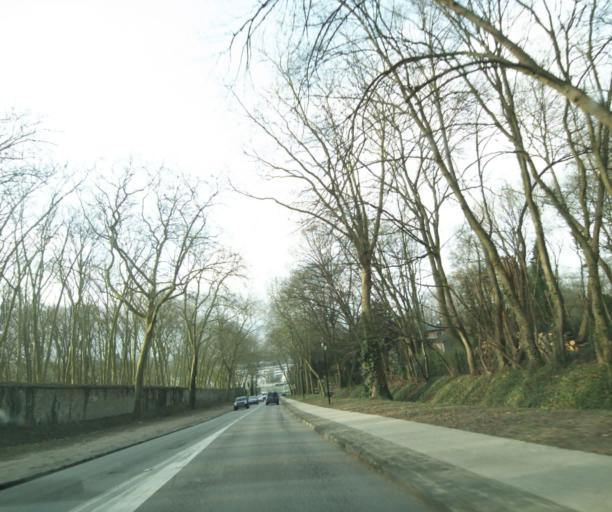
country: FR
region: Ile-de-France
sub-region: Departement des Yvelines
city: Louveciennes
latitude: 48.8645
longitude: 2.1034
